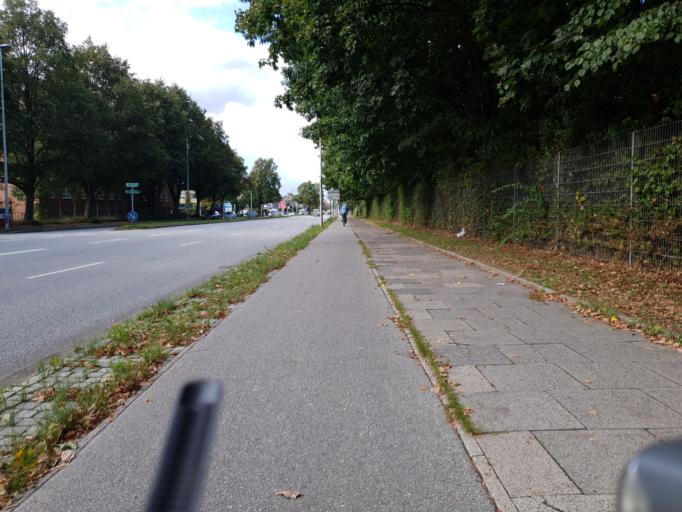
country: DE
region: Schleswig-Holstein
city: Kronshagen
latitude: 54.3384
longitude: 10.1059
